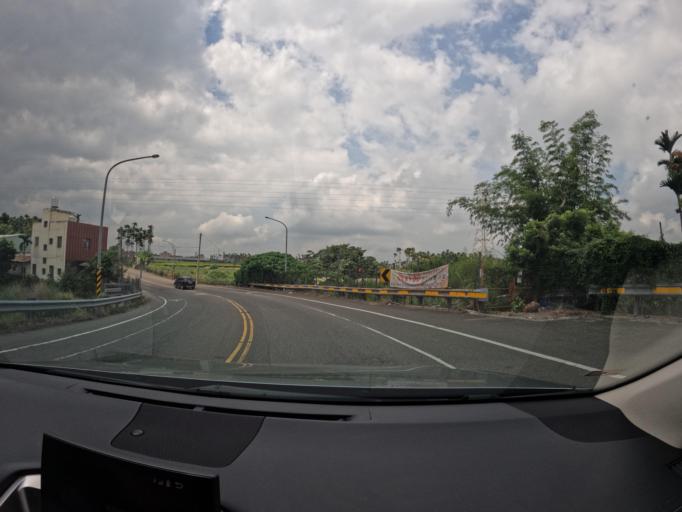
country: TW
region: Taiwan
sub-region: Nantou
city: Nantou
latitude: 23.9226
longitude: 120.6377
